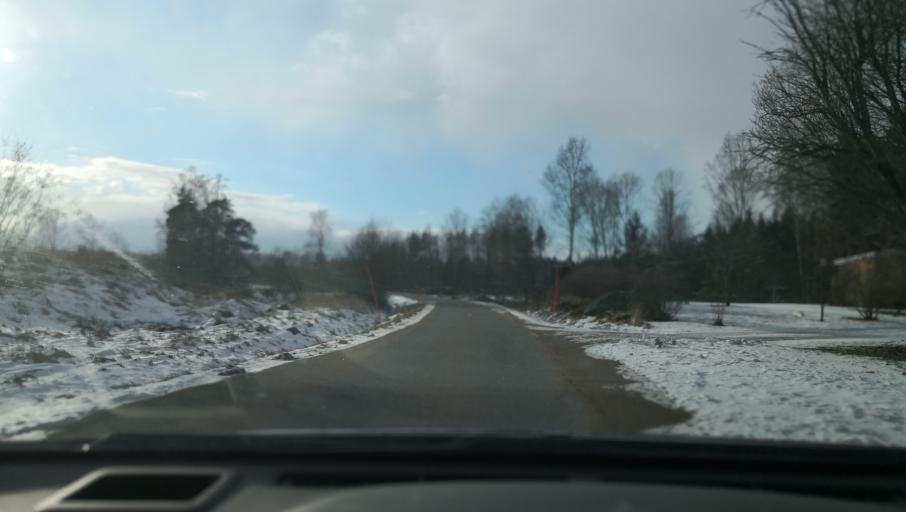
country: SE
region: Uppsala
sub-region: Enkopings Kommun
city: Irsta
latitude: 59.7086
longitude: 16.9007
